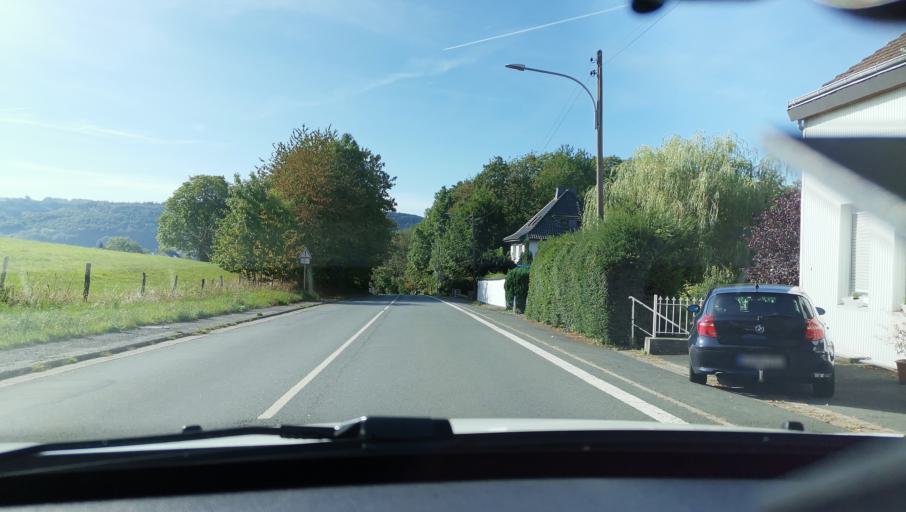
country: DE
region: North Rhine-Westphalia
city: Wetter (Ruhr)
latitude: 51.3475
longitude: 7.3795
